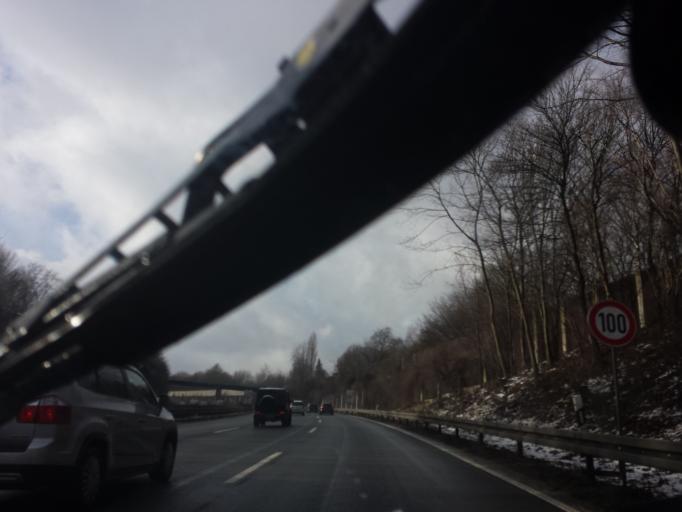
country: DE
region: North Rhine-Westphalia
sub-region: Regierungsbezirk Dusseldorf
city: Solingen
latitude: 51.2254
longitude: 7.0780
